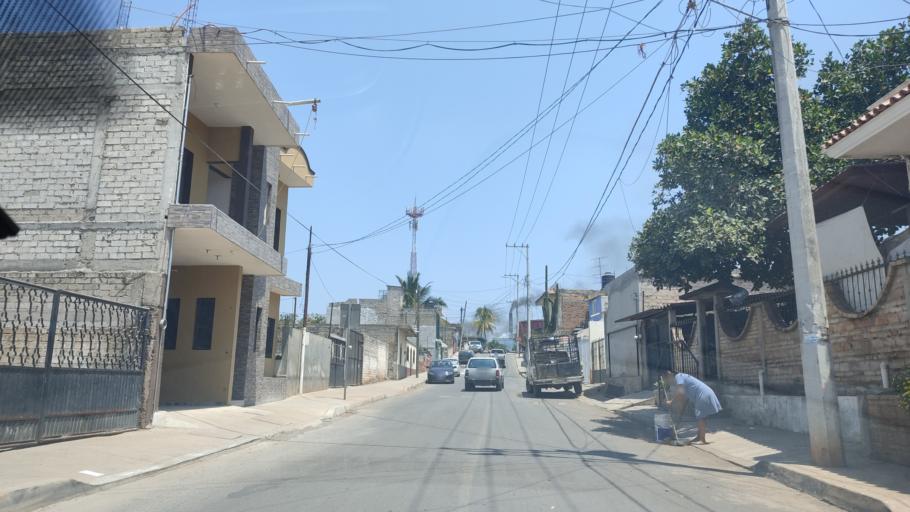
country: MX
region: Nayarit
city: Puga
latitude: 21.5799
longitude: -104.8254
